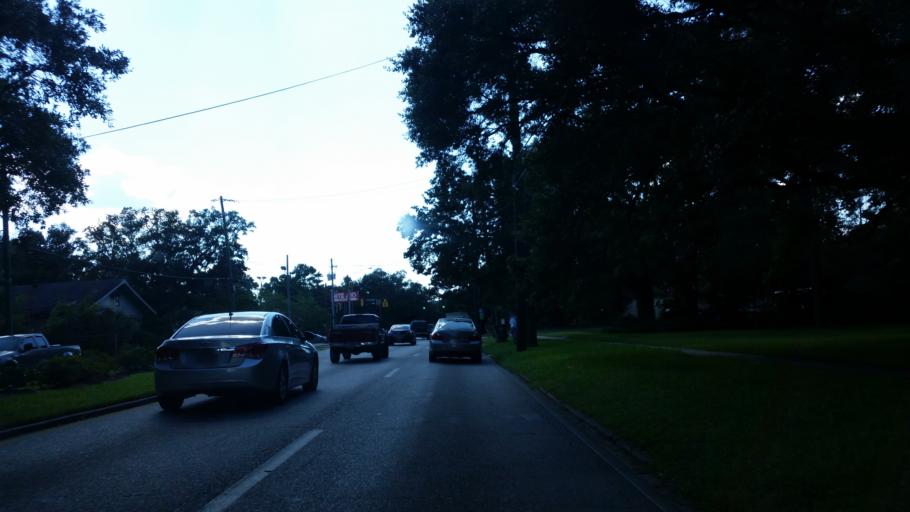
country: US
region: Alabama
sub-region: Mobile County
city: Mobile
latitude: 30.6917
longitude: -88.0869
